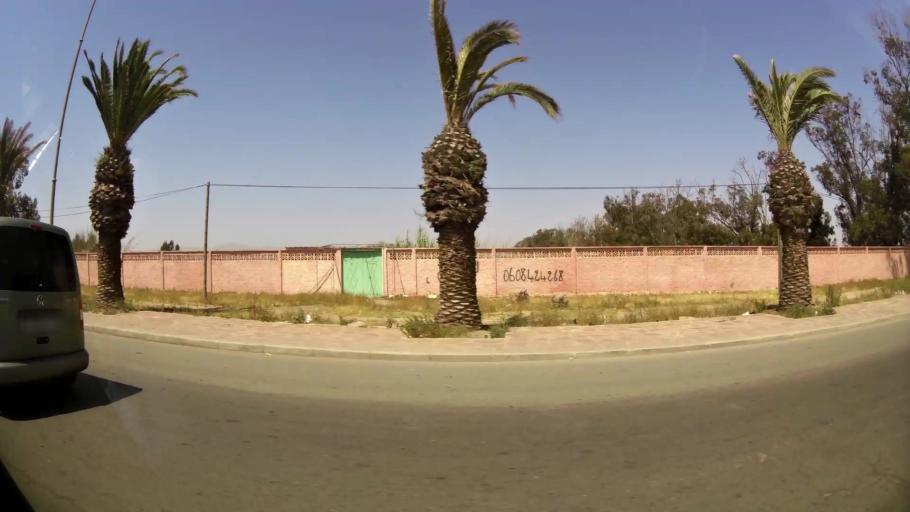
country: MA
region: Souss-Massa-Draa
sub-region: Inezgane-Ait Mellou
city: Inezgane
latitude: 30.3566
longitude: -9.5166
